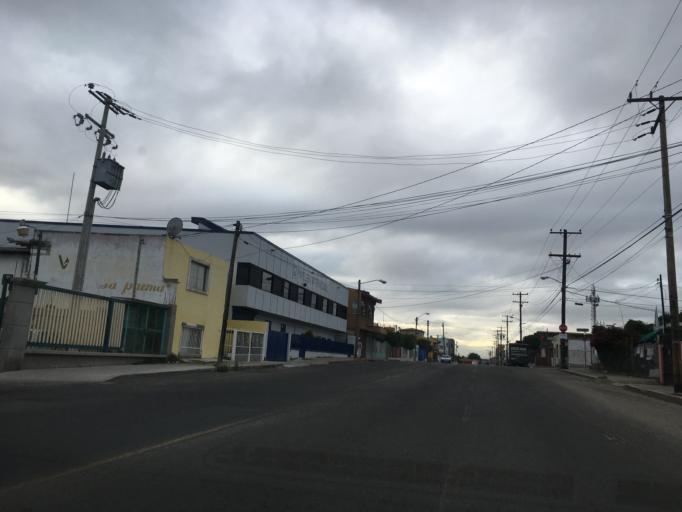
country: MX
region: Baja California
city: Tijuana
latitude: 32.5373
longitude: -117.0548
